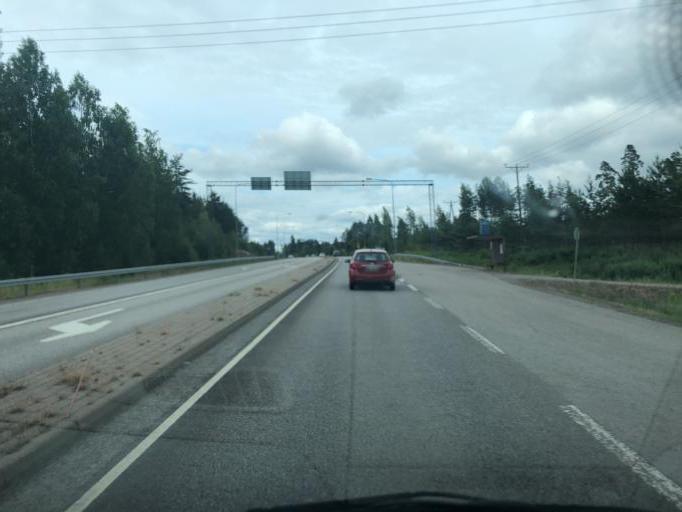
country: FI
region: Kymenlaakso
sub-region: Kouvola
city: Kouvola
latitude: 60.9112
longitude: 26.7633
